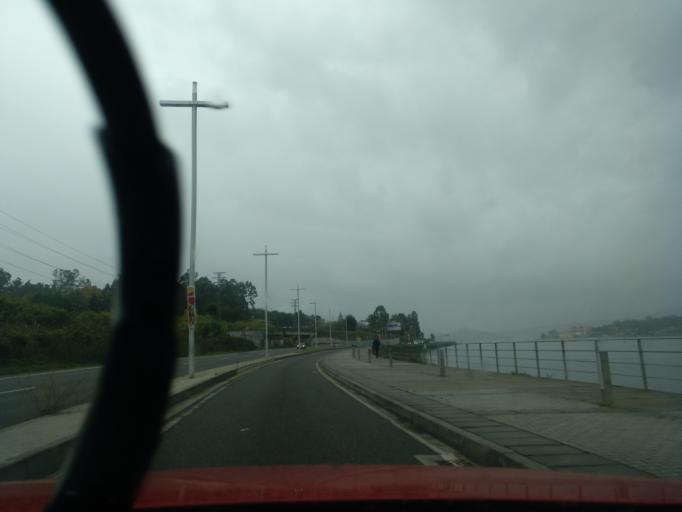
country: ES
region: Galicia
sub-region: Provincia de Pontevedra
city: Poio
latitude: 42.4232
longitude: -8.6564
